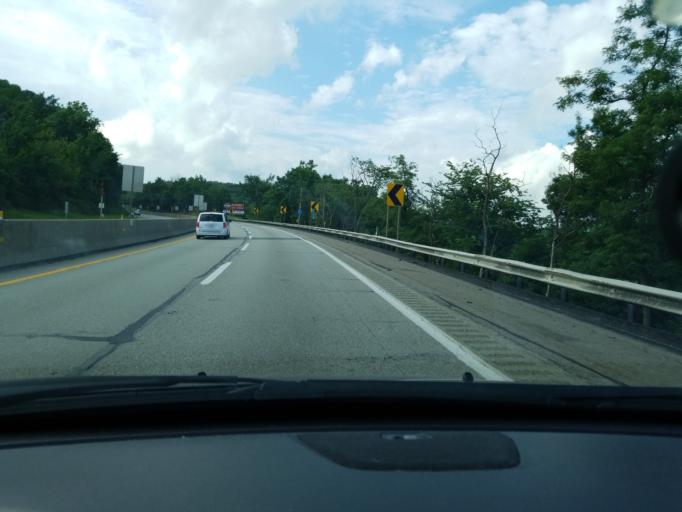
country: US
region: Pennsylvania
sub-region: Beaver County
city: Beaver Falls
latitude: 40.7812
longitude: -80.2397
